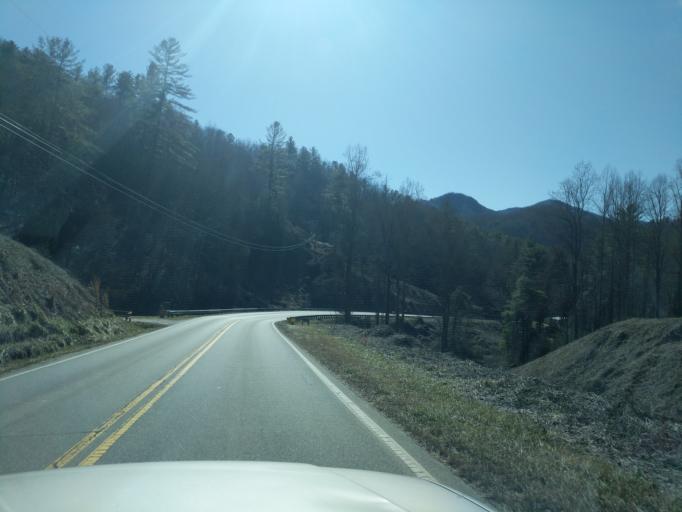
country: US
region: North Carolina
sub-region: Swain County
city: Bryson City
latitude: 35.3327
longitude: -83.5757
